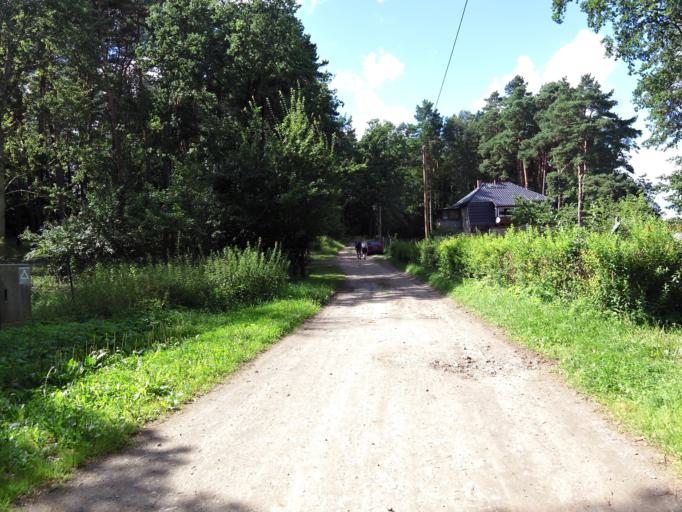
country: DE
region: Brandenburg
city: Lychen
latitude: 53.2137
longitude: 13.2974
